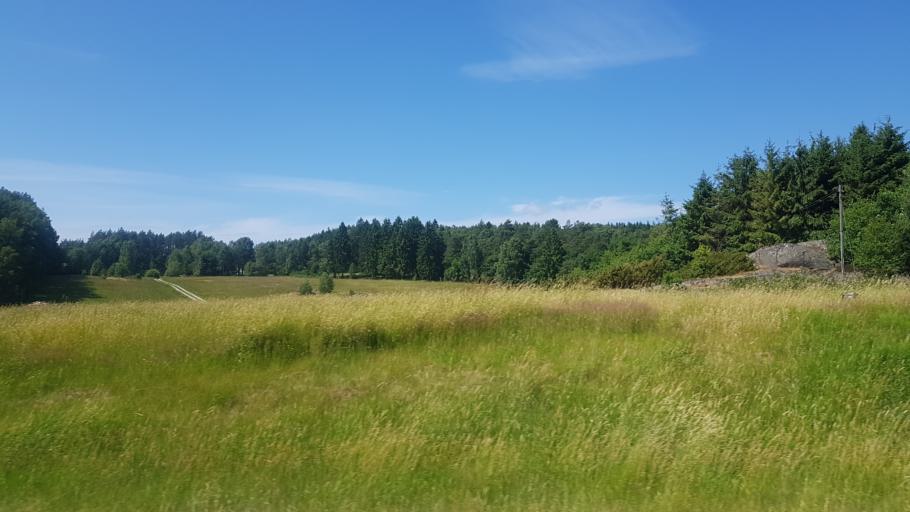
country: SE
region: Vaestra Goetaland
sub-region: Tjorns Kommun
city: Skaerhamn
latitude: 58.0151
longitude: 11.6125
